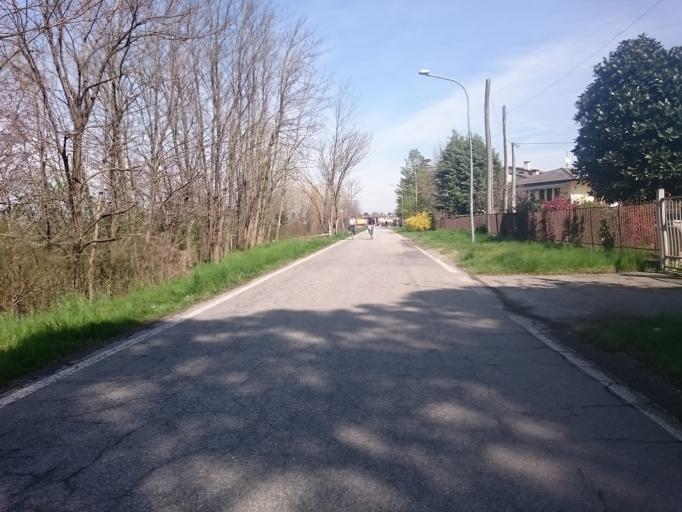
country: IT
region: Veneto
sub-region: Provincia di Padova
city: Limena
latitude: 45.4755
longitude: 11.8400
